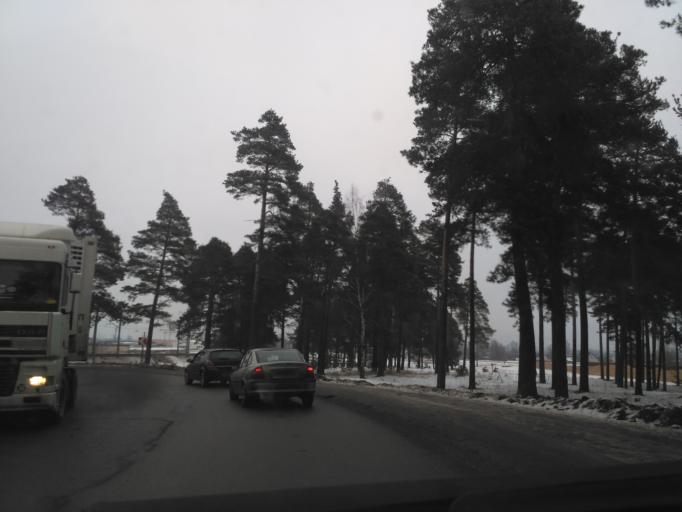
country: BY
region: Minsk
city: Horad Barysaw
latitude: 54.1962
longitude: 28.5151
